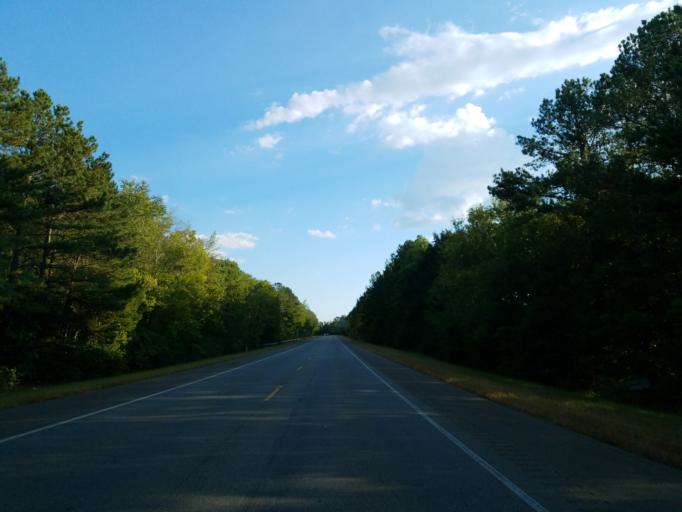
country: US
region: Georgia
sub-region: Murray County
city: Chatsworth
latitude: 34.6597
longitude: -84.7204
